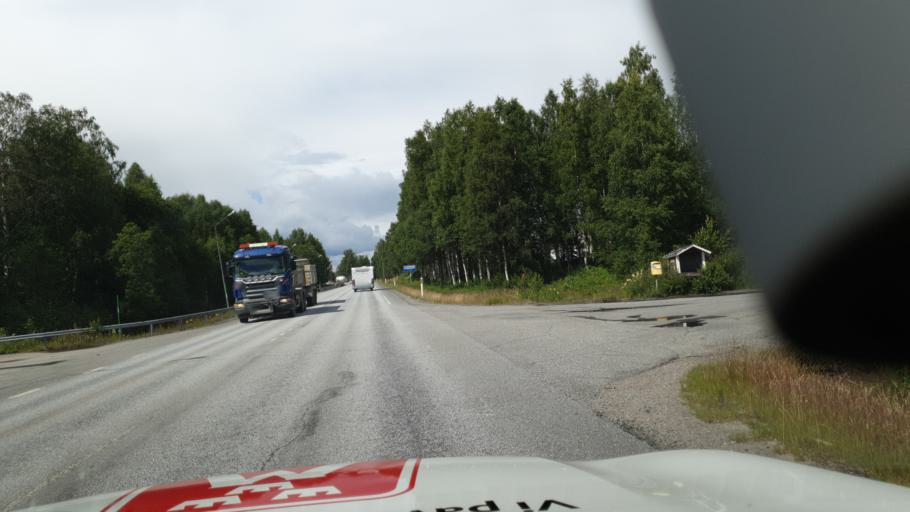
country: SE
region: Vaesterbotten
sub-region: Vannas Kommun
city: Vannasby
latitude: 63.9171
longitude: 19.8762
